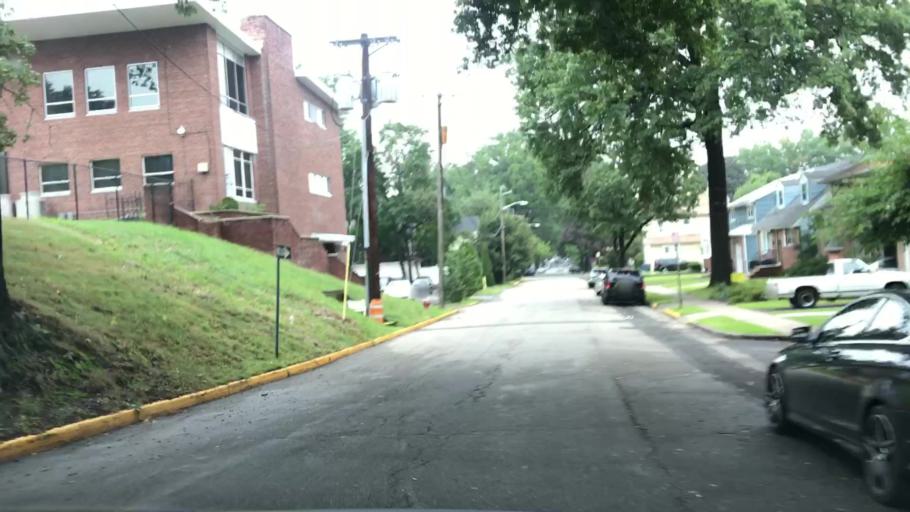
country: US
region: New Jersey
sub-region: Bergen County
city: Rutherford
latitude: 40.8304
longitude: -74.1113
